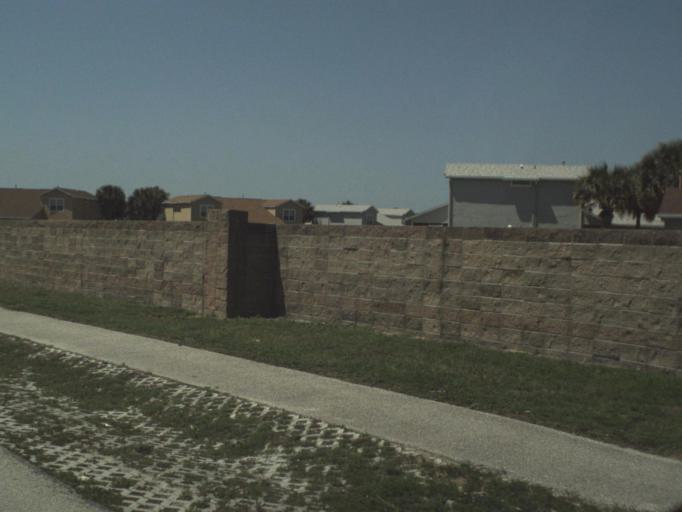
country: US
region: Florida
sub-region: Brevard County
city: South Patrick Shores
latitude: 28.2175
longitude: -80.5987
